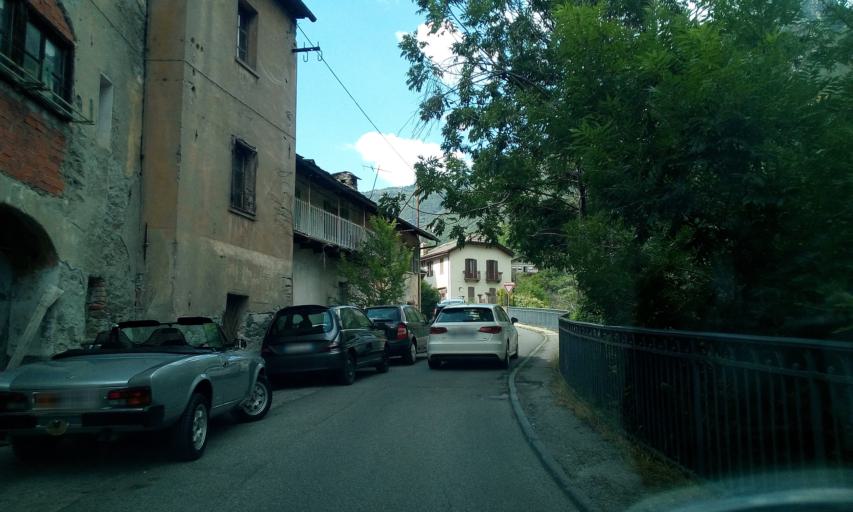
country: IT
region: Aosta Valley
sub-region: Valle d'Aosta
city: Chatillon
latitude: 45.7495
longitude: 7.6088
